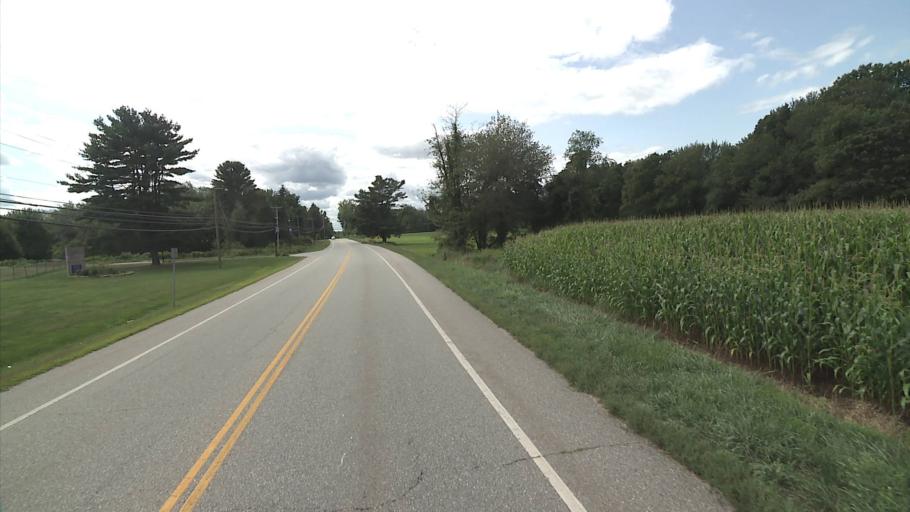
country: US
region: Connecticut
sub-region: Windham County
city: South Windham
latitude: 41.6258
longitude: -72.2406
